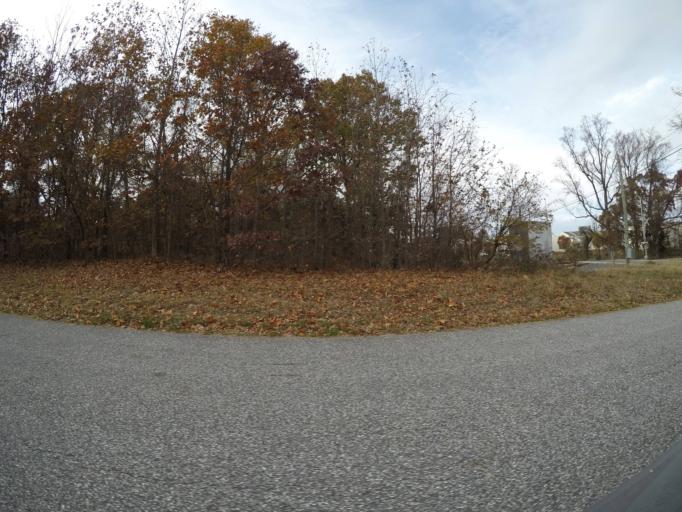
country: US
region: Maryland
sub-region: Harford County
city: Havre de Grace
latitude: 39.5468
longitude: -76.1085
